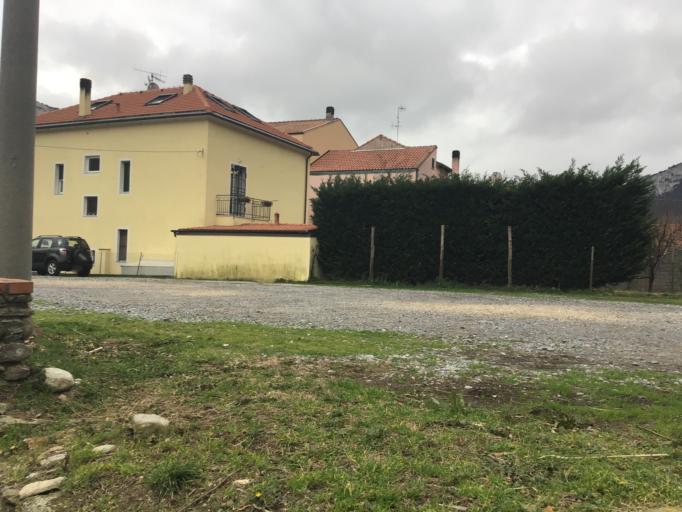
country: IT
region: Liguria
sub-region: Provincia di Savona
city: Orco Feglino
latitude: 44.2195
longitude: 8.3235
